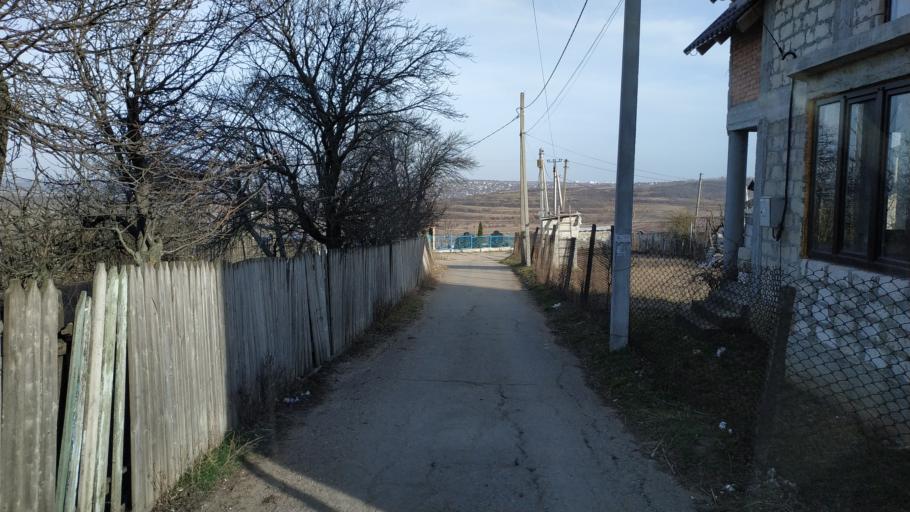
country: MD
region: Chisinau
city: Vatra
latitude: 47.0645
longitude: 28.6900
